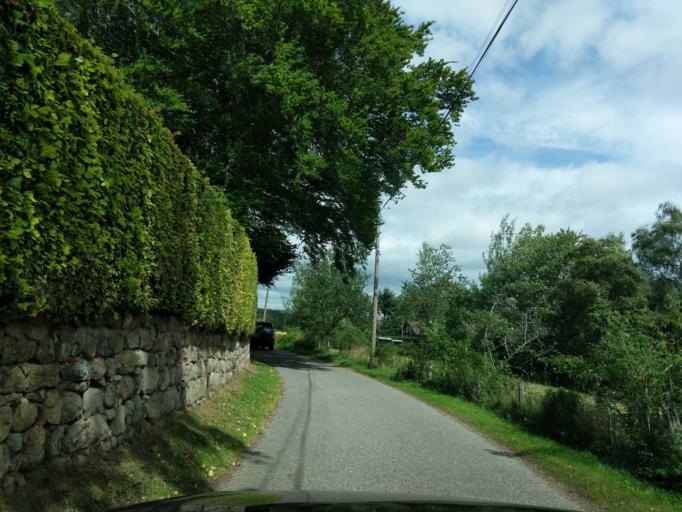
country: GB
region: Scotland
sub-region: Aberdeenshire
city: Aboyne
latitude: 57.0613
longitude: -2.7321
